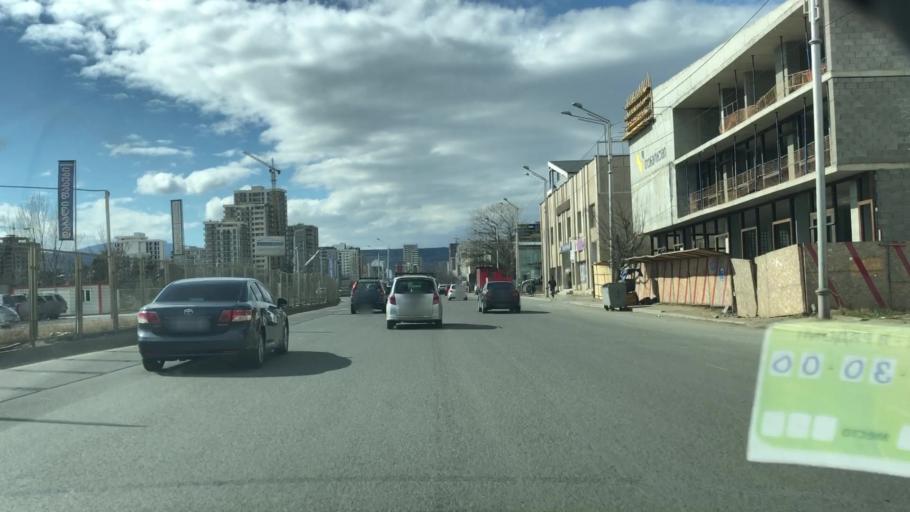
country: GE
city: Zahesi
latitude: 41.7879
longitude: 44.7731
